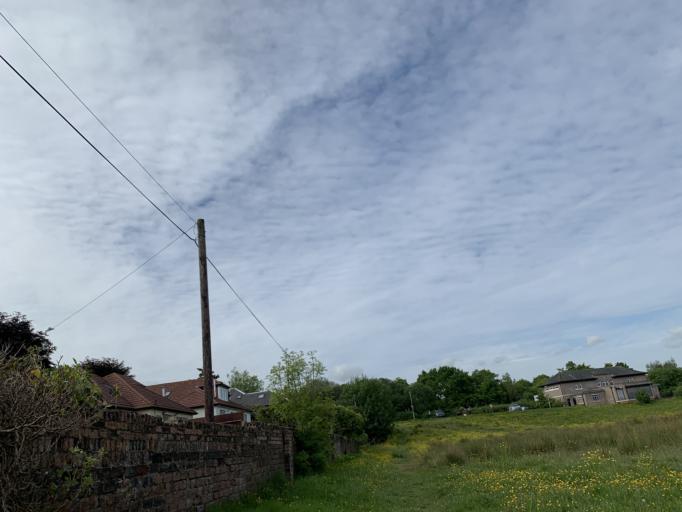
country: GB
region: Scotland
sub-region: East Renfrewshire
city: Giffnock
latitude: 55.8032
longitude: -4.3035
